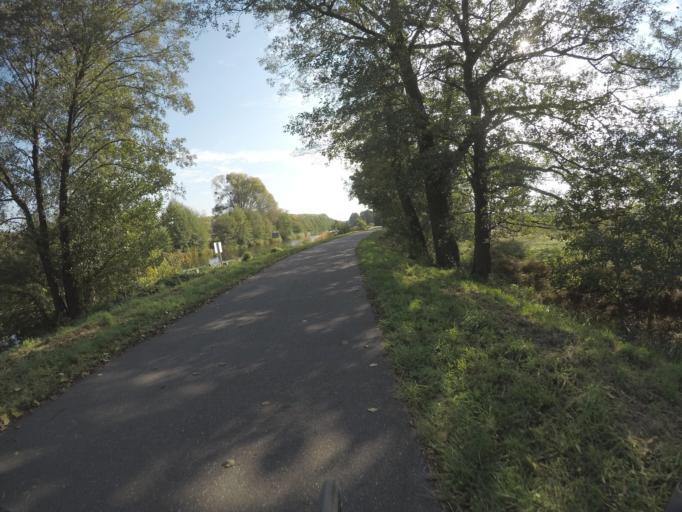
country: DE
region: Brandenburg
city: Oranienburg
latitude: 52.7153
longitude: 13.2379
